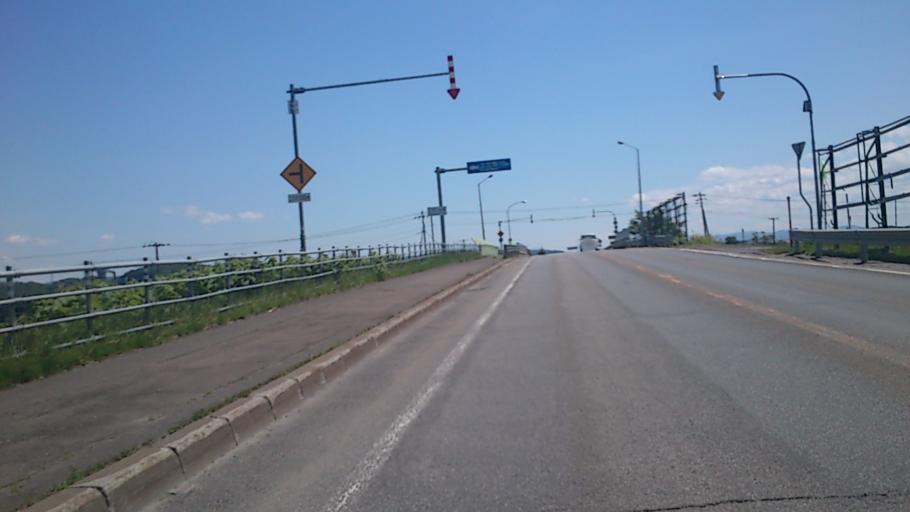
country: JP
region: Hokkaido
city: Nayoro
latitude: 44.1969
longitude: 142.3948
